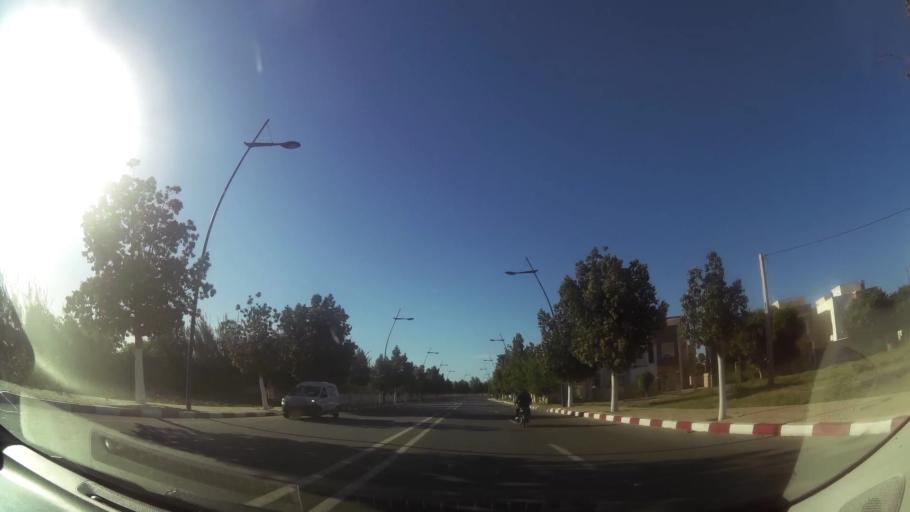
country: MA
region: Oriental
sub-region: Berkane-Taourirt
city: Madagh
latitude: 35.0710
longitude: -2.2177
